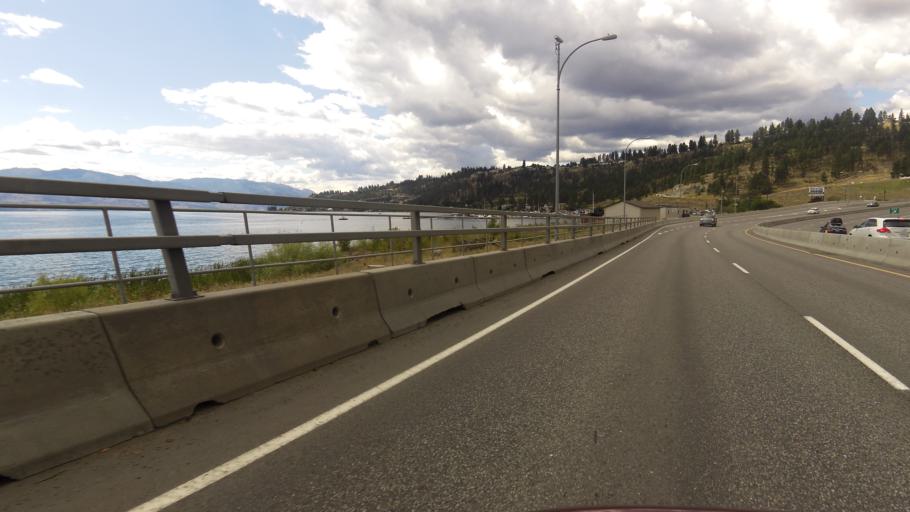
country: CA
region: British Columbia
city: Kelowna
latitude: 49.8780
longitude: -119.5207
